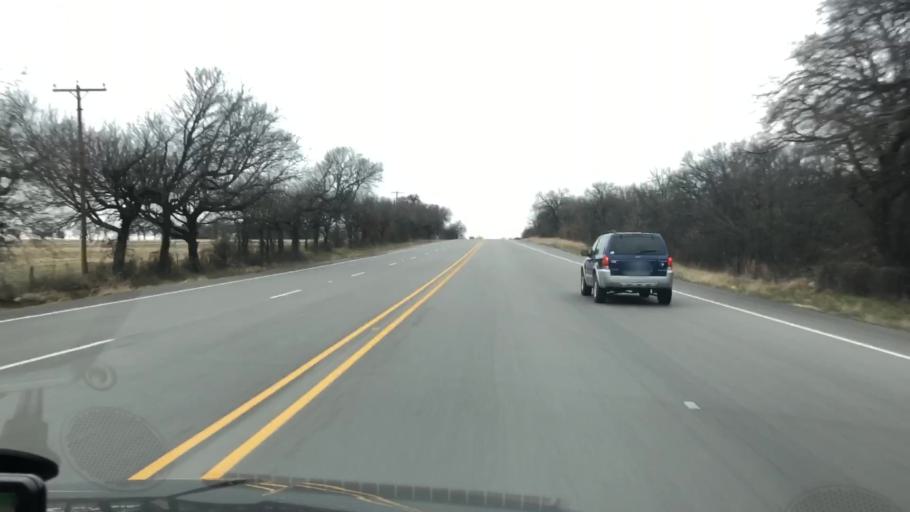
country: US
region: Texas
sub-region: Hamilton County
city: Hico
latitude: 32.0121
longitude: -98.0628
